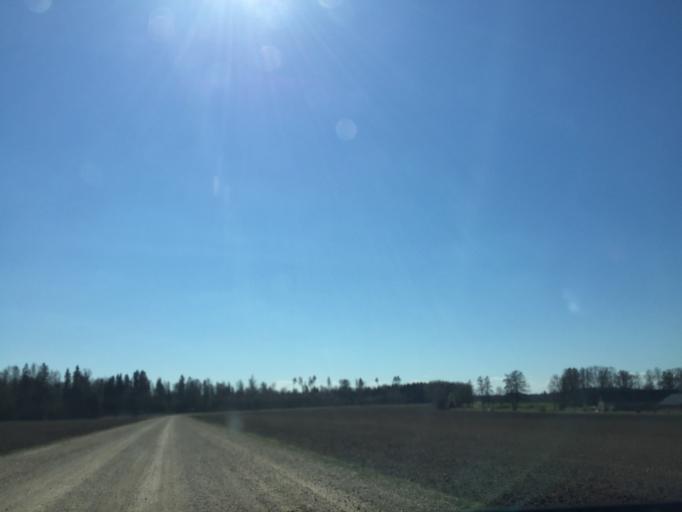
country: EE
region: Viljandimaa
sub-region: Viiratsi vald
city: Viiratsi
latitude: 58.3444
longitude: 25.7212
